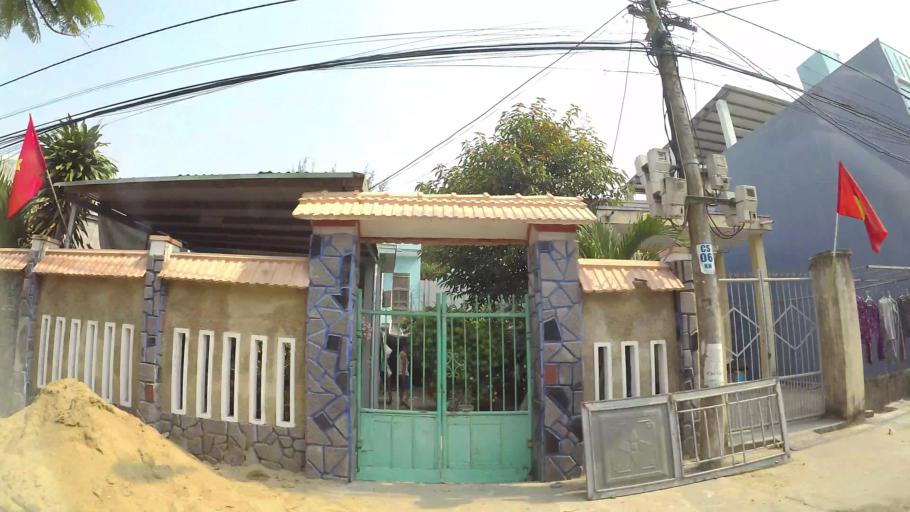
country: VN
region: Da Nang
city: Ngu Hanh Son
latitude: 15.9904
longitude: 108.2446
